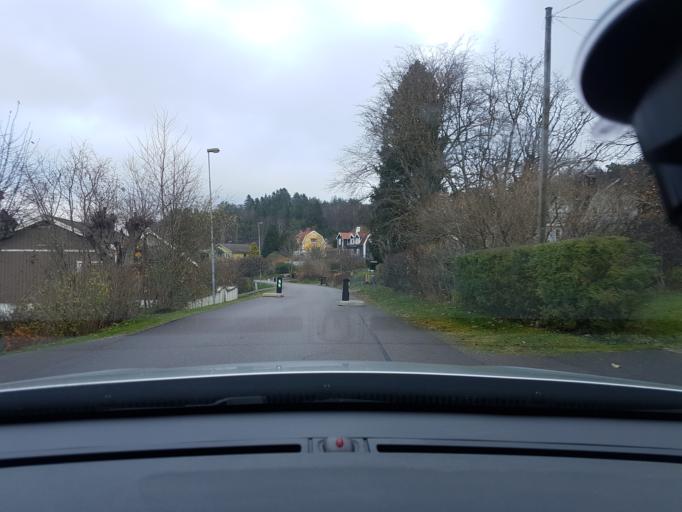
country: SE
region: Vaestra Goetaland
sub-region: Ale Kommun
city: Alafors
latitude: 57.9192
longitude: 12.0732
